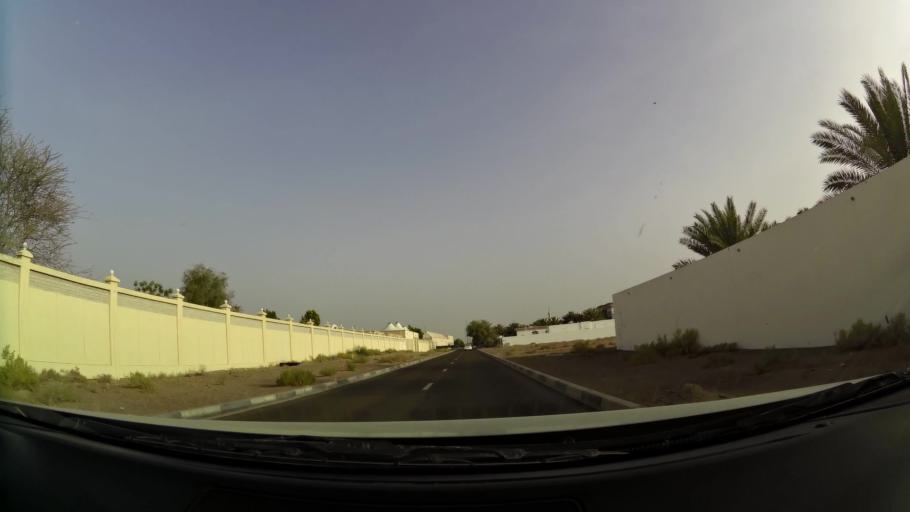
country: AE
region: Abu Dhabi
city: Al Ain
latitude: 24.2403
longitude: 55.7234
